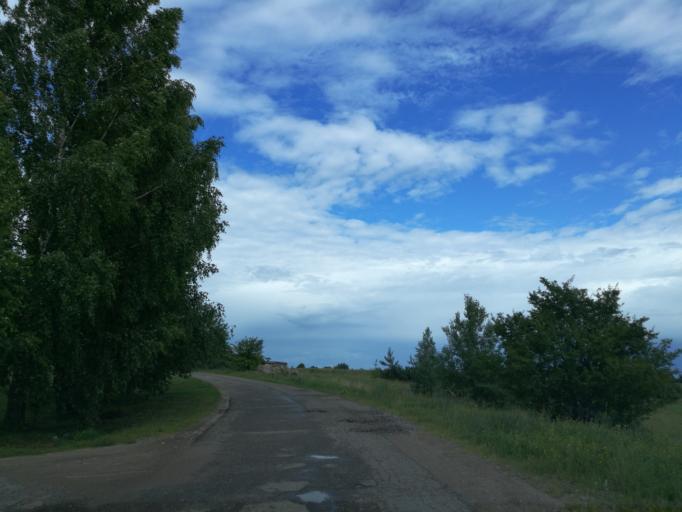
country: LT
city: Lentvaris
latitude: 54.6750
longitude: 25.0190
